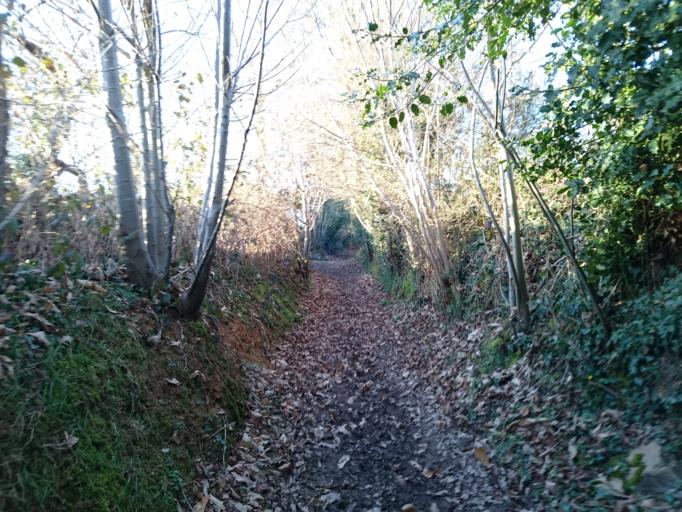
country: FR
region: Brittany
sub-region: Departement d'Ille-et-Vilaine
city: Chanteloup
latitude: 47.9362
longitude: -1.6096
